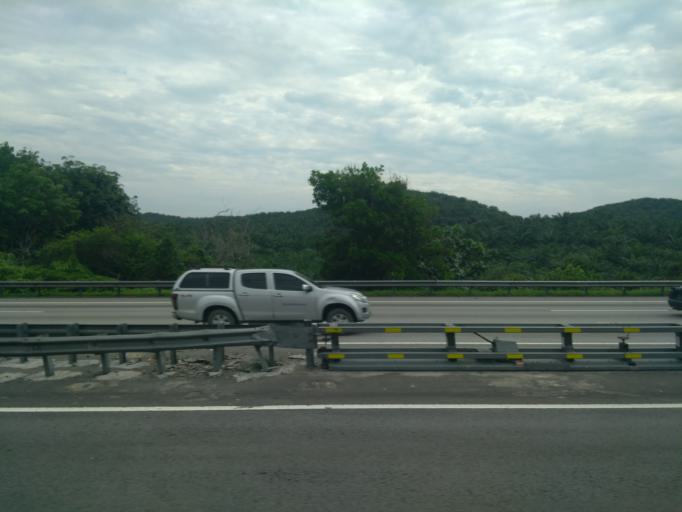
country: MY
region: Negeri Sembilan
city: Seremban
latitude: 2.6579
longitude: 101.9872
